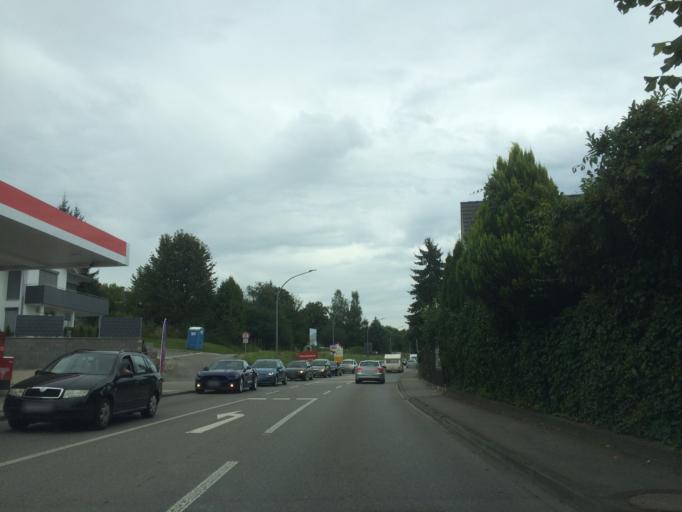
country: DE
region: Baden-Wuerttemberg
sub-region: Tuebingen Region
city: Markdorf
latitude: 47.7191
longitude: 9.3963
